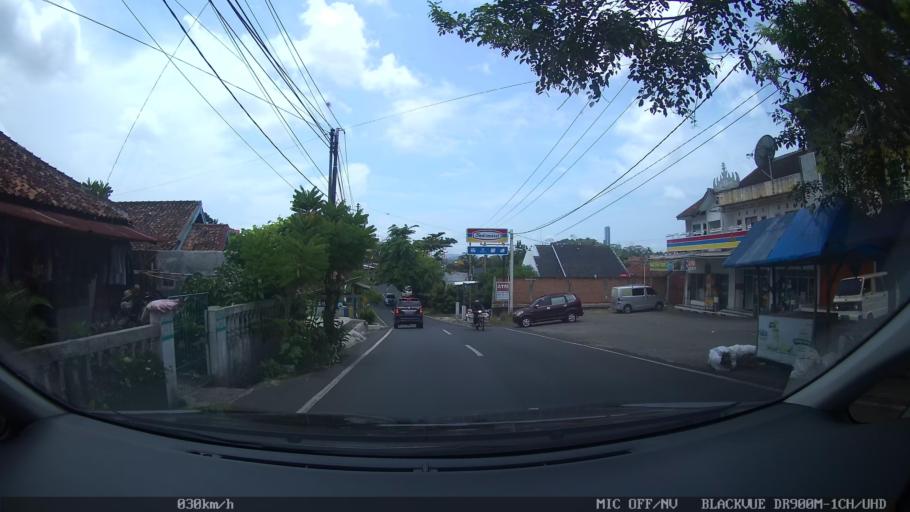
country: ID
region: Lampung
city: Bandarlampung
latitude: -5.4118
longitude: 105.2410
